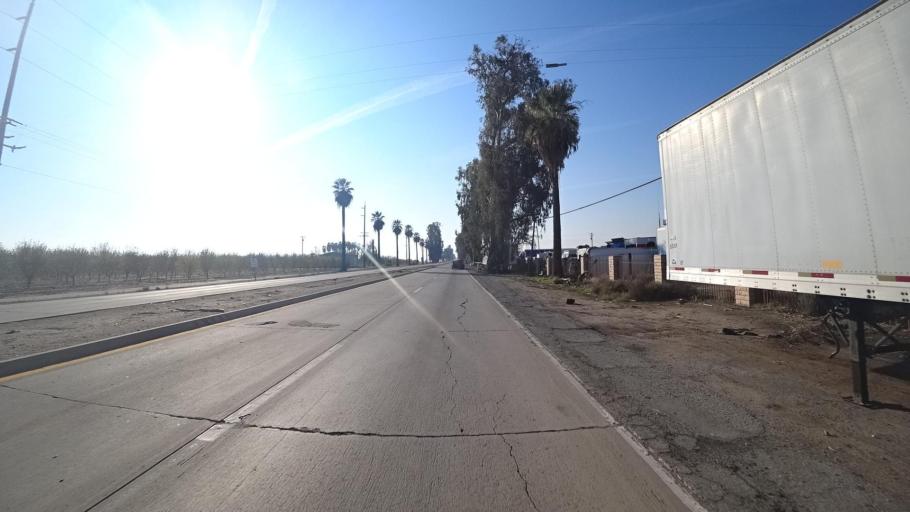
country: US
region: California
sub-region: Kern County
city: Greenfield
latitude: 35.2303
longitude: -119.0032
